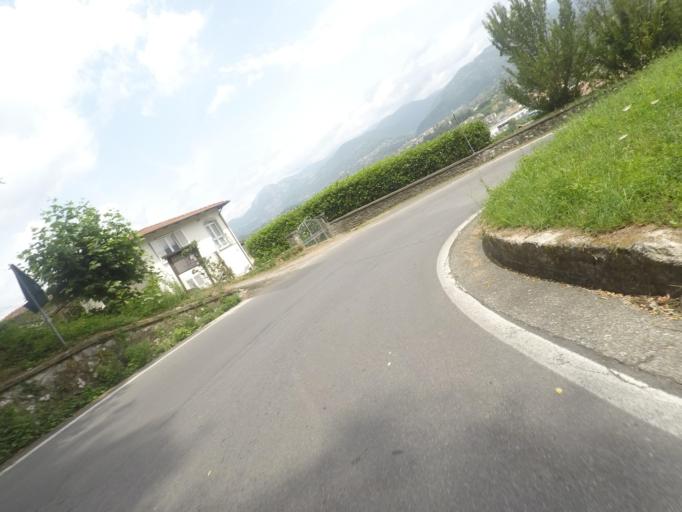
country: IT
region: Tuscany
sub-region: Provincia di Lucca
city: Castelnuovo di Garfagnana
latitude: 44.1104
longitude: 10.4039
